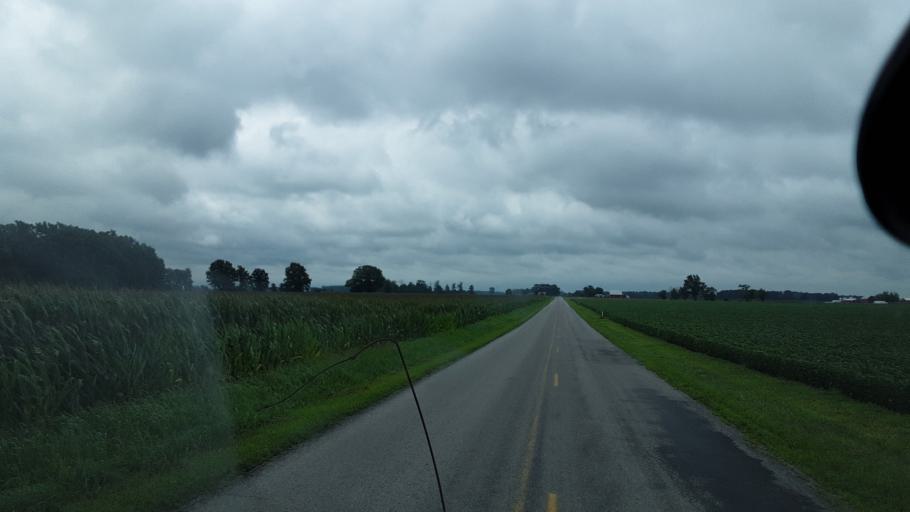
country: US
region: Indiana
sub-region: Wells County
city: Ossian
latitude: 40.8849
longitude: -85.1092
